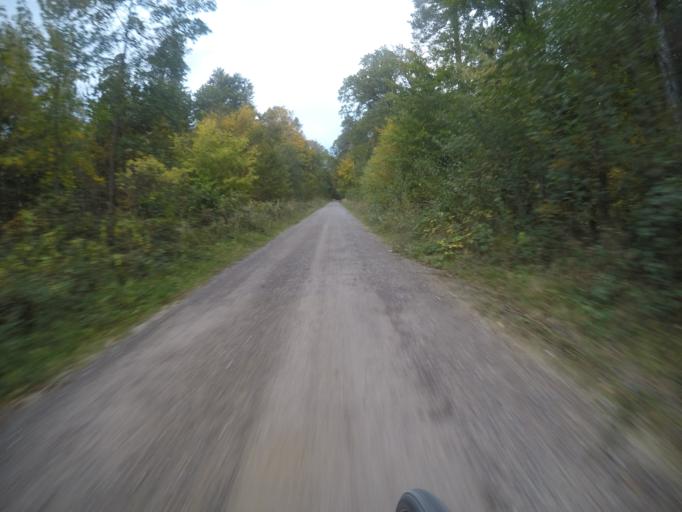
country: DE
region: Baden-Wuerttemberg
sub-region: Regierungsbezirk Stuttgart
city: Schonaich
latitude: 48.6948
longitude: 9.0642
